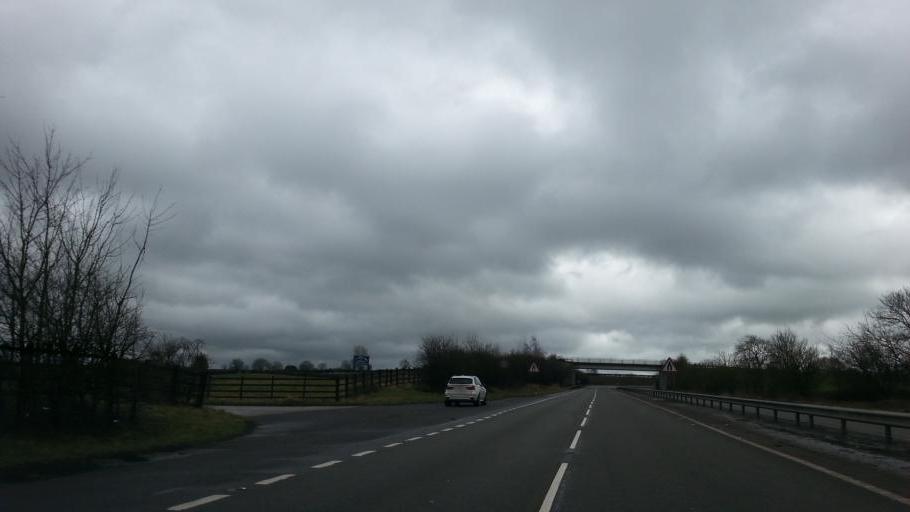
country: GB
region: England
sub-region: Leicestershire
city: Kibworth Harcourt
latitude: 52.5550
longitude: -1.0087
